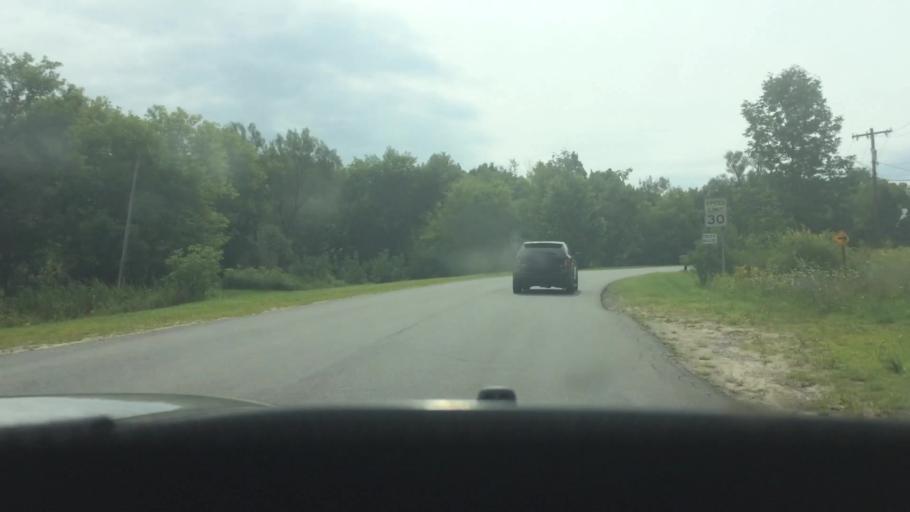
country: US
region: New York
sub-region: St. Lawrence County
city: Canton
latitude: 44.4697
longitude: -75.2335
